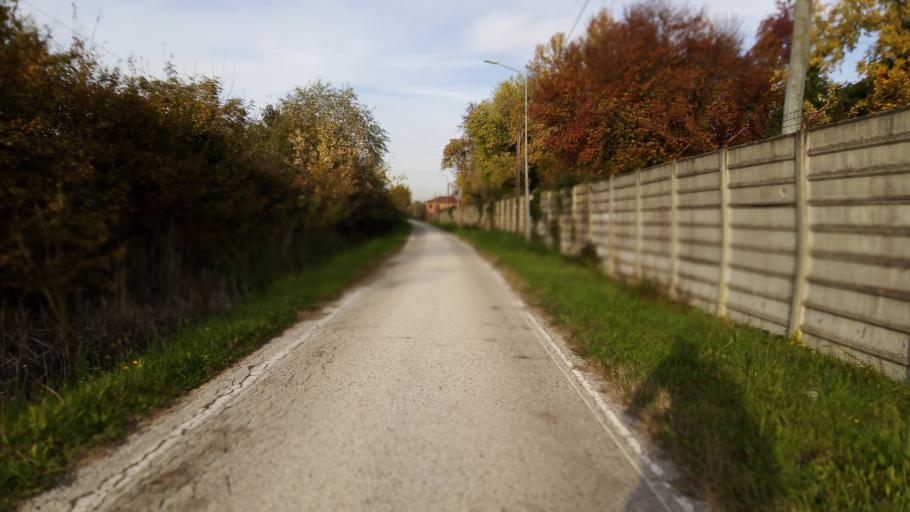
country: IT
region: Veneto
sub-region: Provincia di Padova
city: Abano Terme
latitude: 45.3605
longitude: 11.8153
